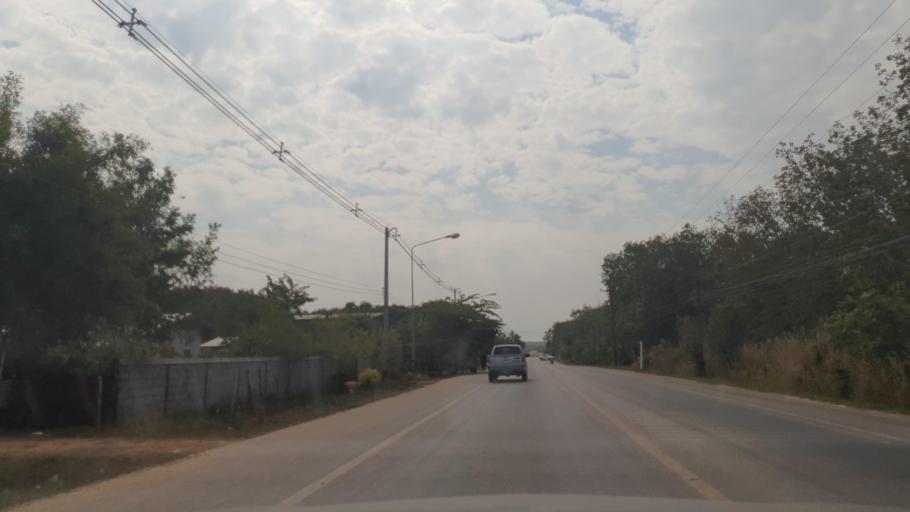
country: TH
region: Changwat Bueng Kan
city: Si Wilai
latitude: 18.2984
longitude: 103.8022
